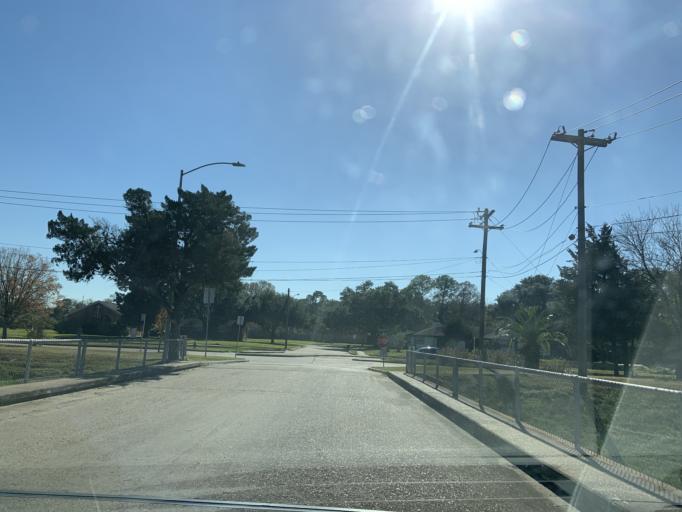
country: US
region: Texas
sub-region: Fort Bend County
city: Missouri City
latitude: 29.6736
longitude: -95.5158
